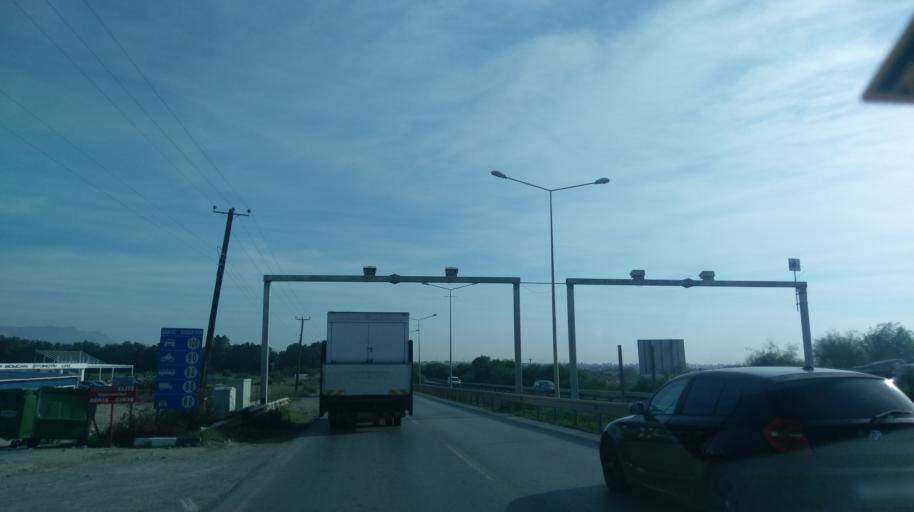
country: CY
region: Lefkosia
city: Nicosia
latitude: 35.2128
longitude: 33.3853
